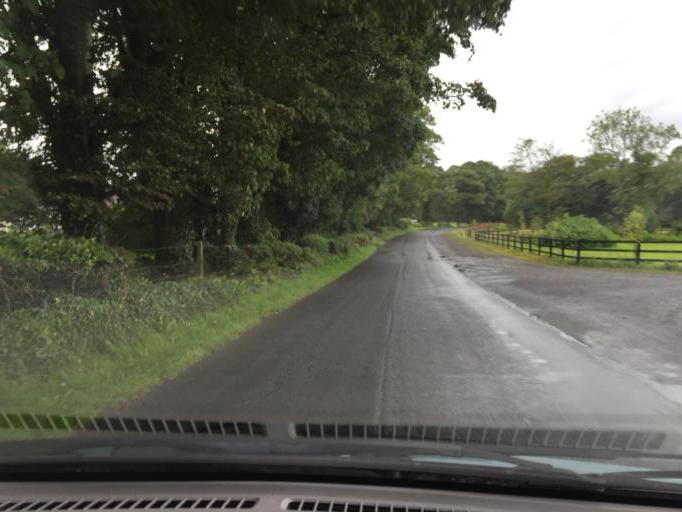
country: IE
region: Connaught
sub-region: Maigh Eo
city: Swinford
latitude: 54.0358
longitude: -8.8895
